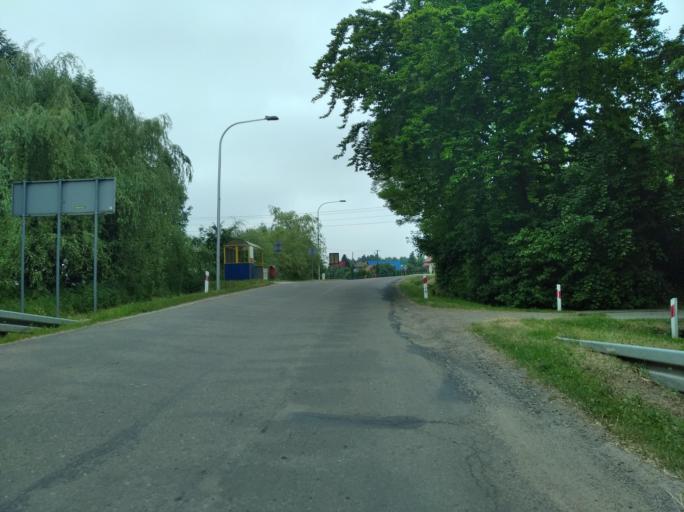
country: PL
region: Subcarpathian Voivodeship
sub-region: Powiat krosnienski
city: Sieniawa
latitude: 49.5798
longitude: 21.9240
